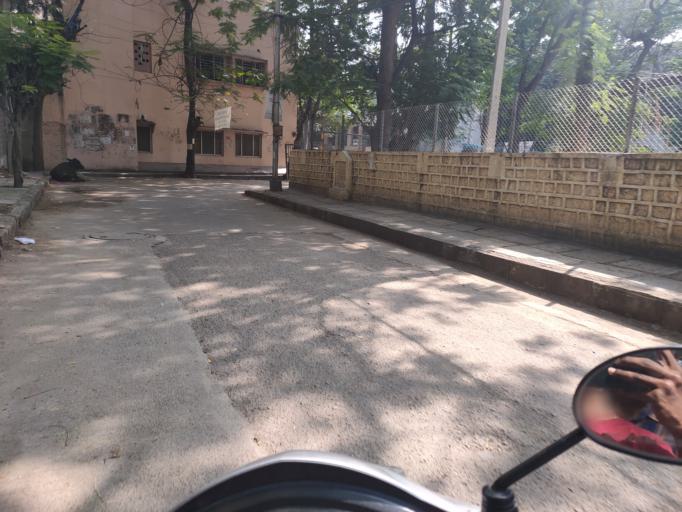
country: IN
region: Telangana
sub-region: Hyderabad
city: Malkajgiri
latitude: 17.4382
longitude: 78.4835
